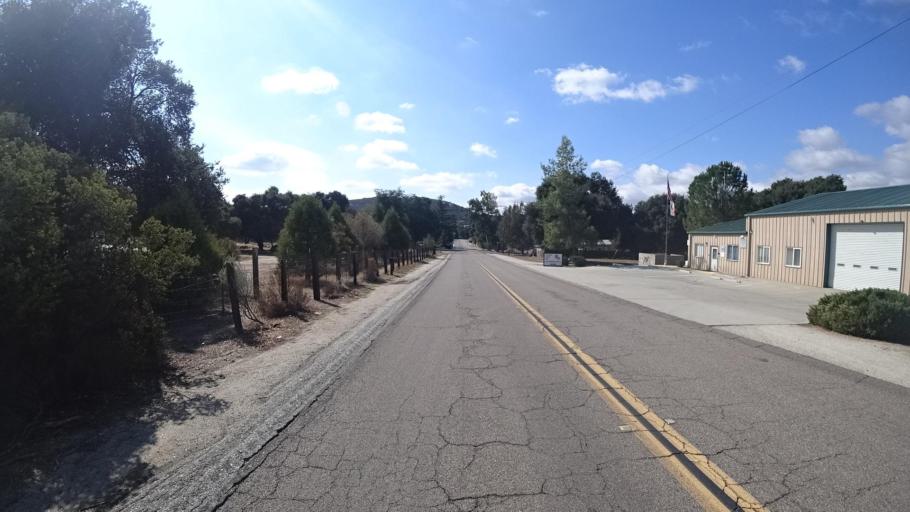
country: US
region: California
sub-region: San Diego County
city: Campo
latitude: 32.6792
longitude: -116.5074
